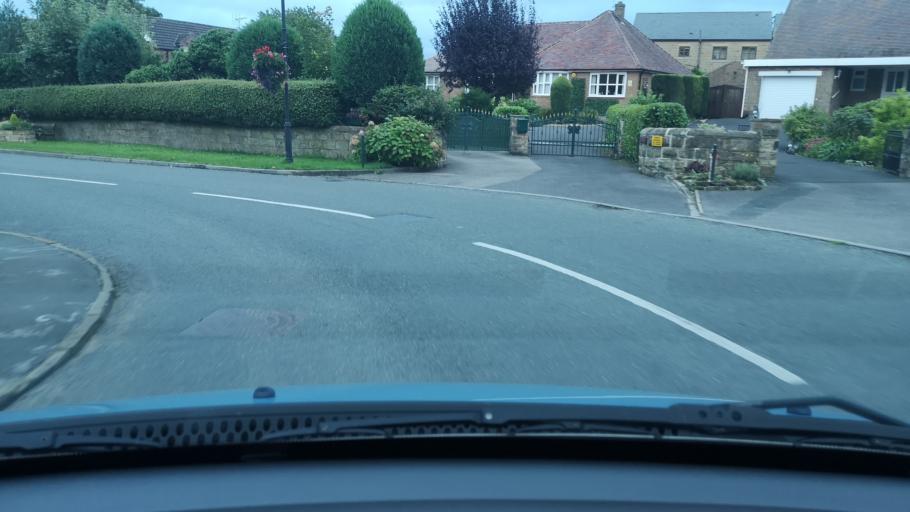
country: GB
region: England
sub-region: City and Borough of Wakefield
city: Badsworth
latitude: 53.6288
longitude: -1.3012
